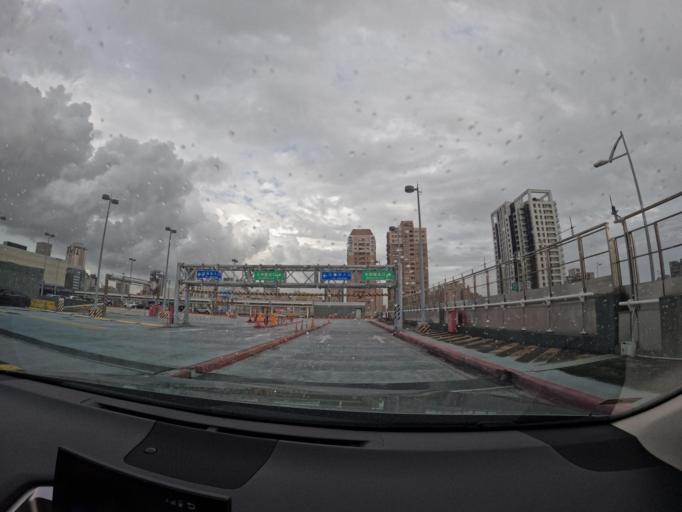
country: TW
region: Kaohsiung
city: Kaohsiung
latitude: 22.6865
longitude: 120.3059
